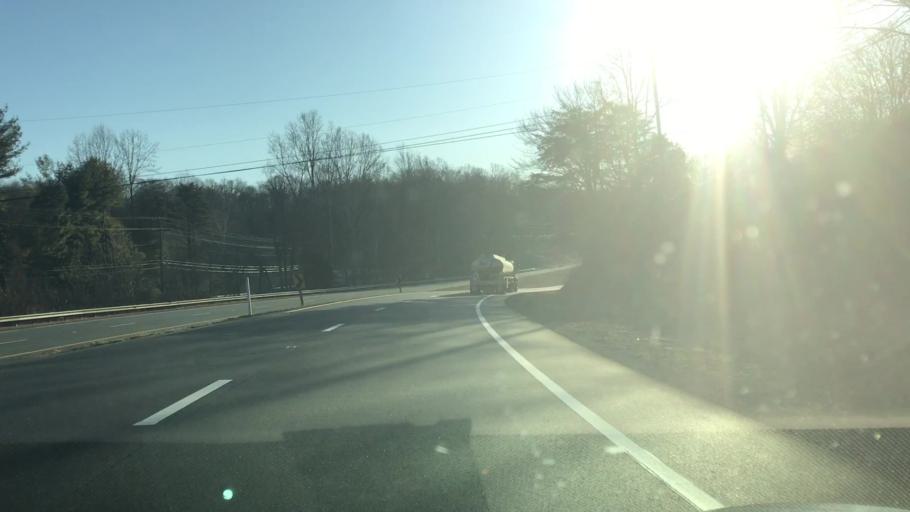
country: US
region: Virginia
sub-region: Botetourt County
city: Blue Ridge
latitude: 37.3971
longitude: -79.7516
